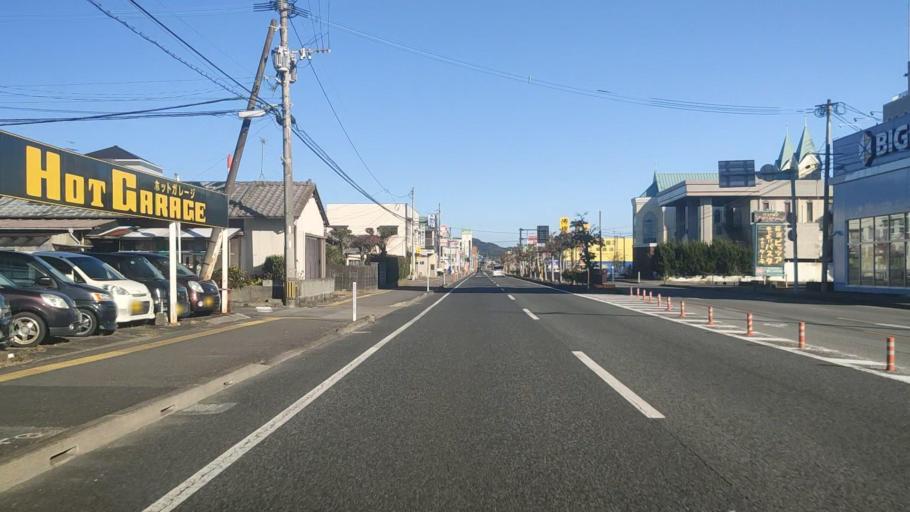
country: JP
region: Miyazaki
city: Nobeoka
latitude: 32.5906
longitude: 131.6759
